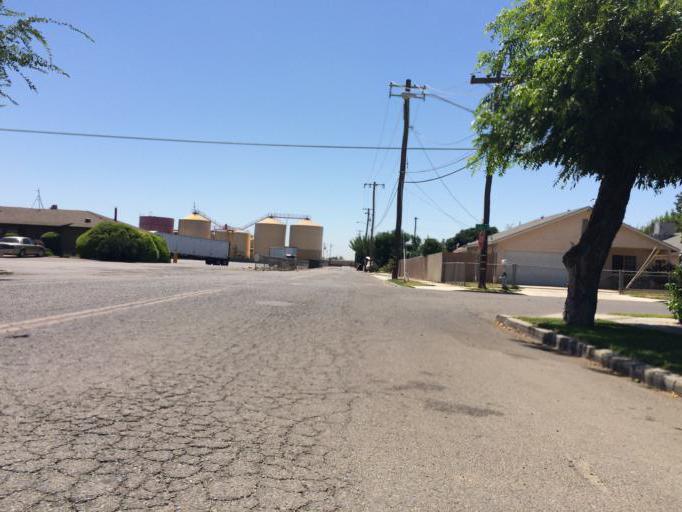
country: US
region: California
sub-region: Fresno County
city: Fresno
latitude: 36.7036
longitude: -119.7548
